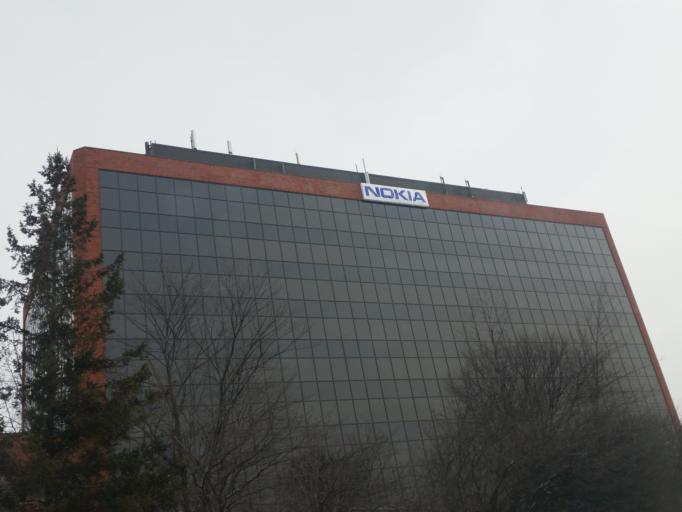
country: CA
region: Ontario
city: Bells Corners
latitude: 45.3480
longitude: -75.9222
